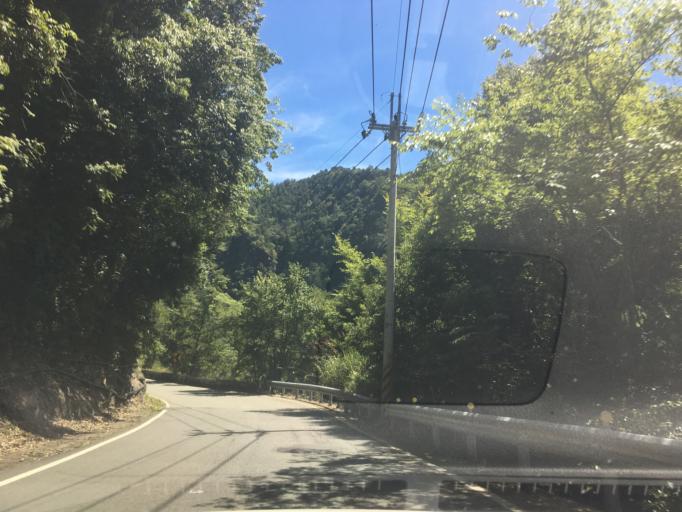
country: TW
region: Taiwan
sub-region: Nantou
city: Puli
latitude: 24.2197
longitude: 121.2645
